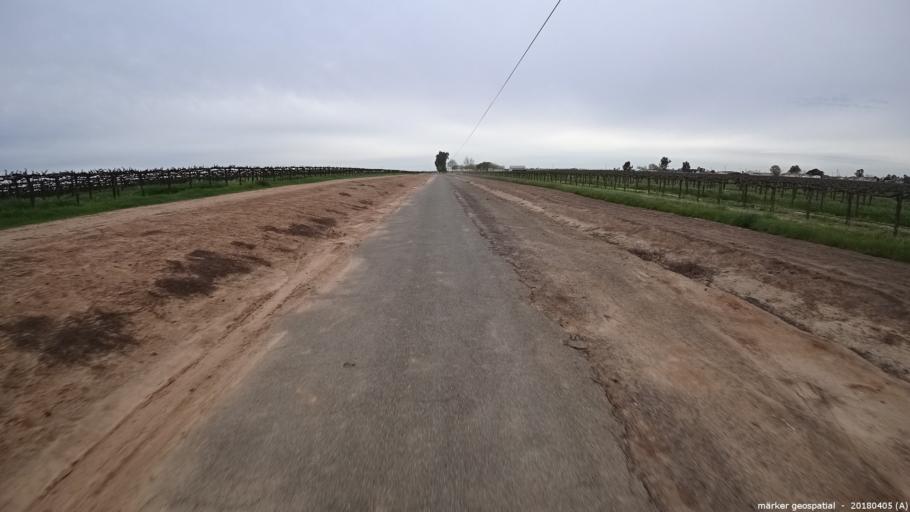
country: US
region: California
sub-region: Sacramento County
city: Herald
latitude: 38.3176
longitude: -121.2374
